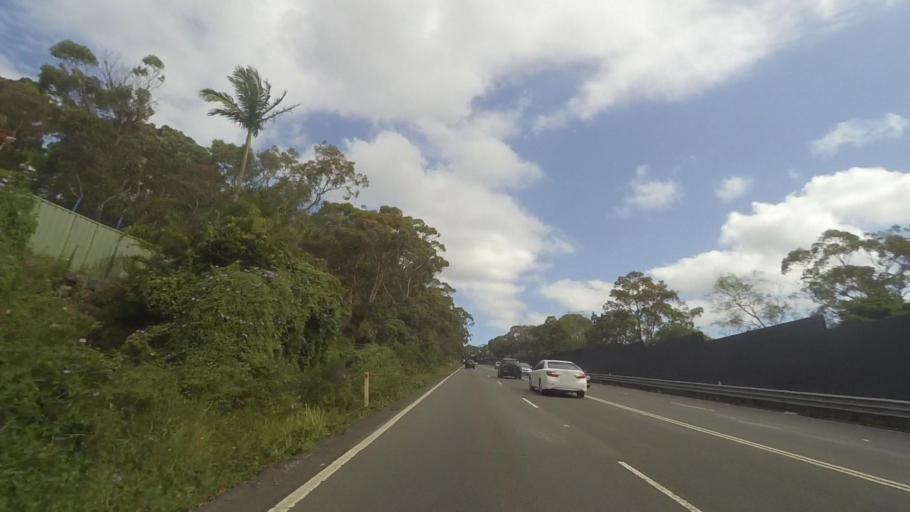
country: AU
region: New South Wales
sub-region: Sutherland Shire
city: Heathcote
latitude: -34.0765
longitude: 151.0075
